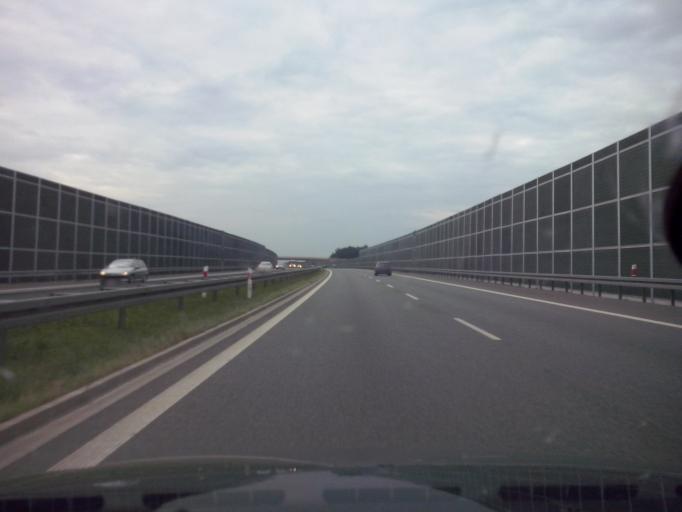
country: PL
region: Lesser Poland Voivodeship
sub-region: Powiat bochenski
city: Bochnia
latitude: 50.0040
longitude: 20.4101
